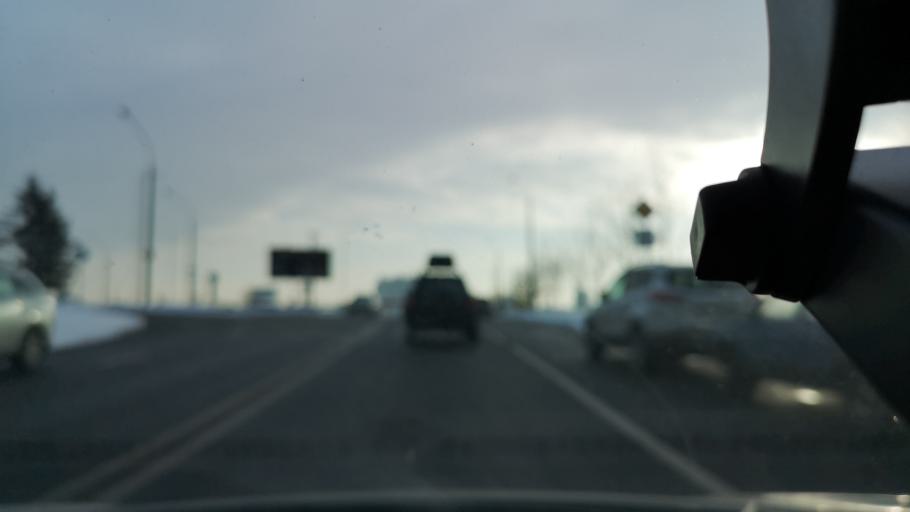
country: BY
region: Minsk
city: Borovlyany
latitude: 53.9450
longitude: 27.6659
